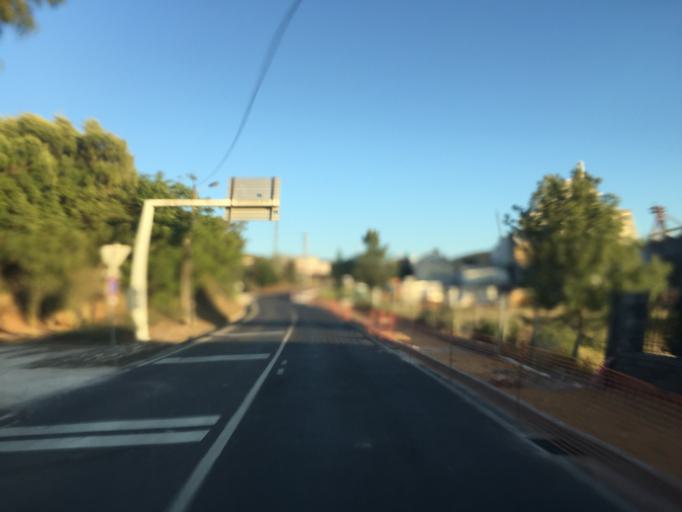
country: PT
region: Lisbon
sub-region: Torres Vedras
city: Torres Vedras
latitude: 39.0744
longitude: -9.2507
